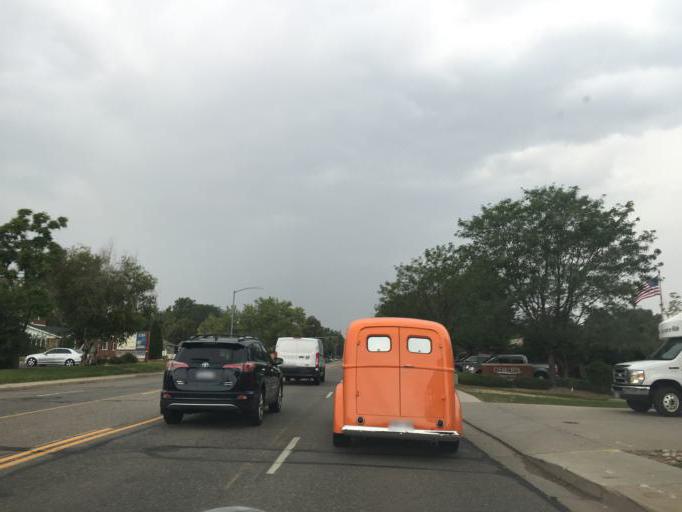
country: US
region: Colorado
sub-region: Jefferson County
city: Wheat Ridge
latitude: 39.7694
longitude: -105.0836
